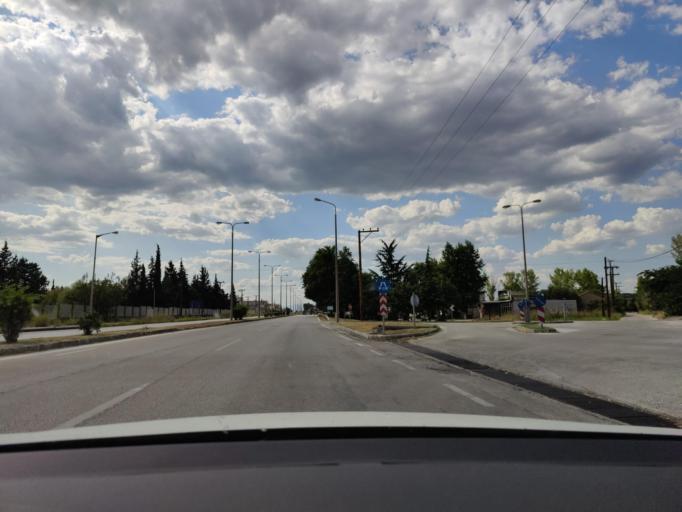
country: GR
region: Central Macedonia
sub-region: Nomos Serron
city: Lefkonas
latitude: 41.0946
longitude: 23.5050
